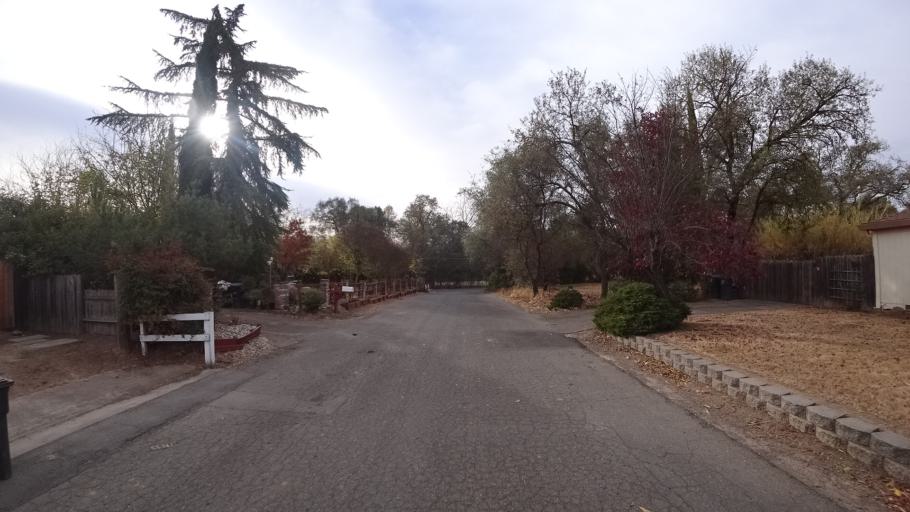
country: US
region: California
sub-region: Sacramento County
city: Citrus Heights
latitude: 38.7117
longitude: -121.2838
